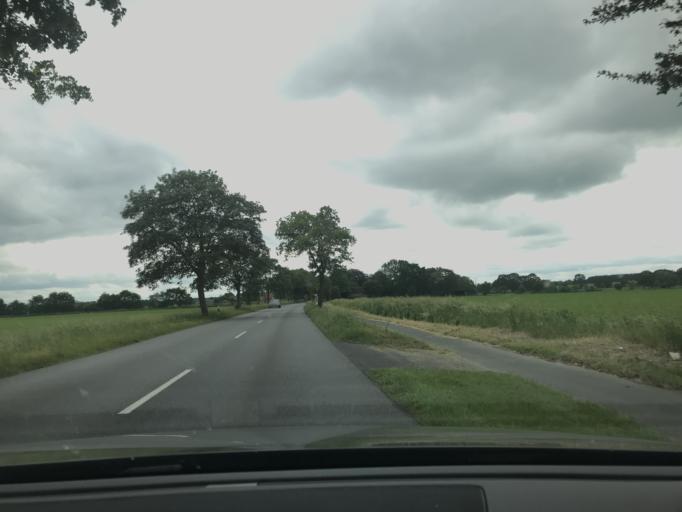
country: DE
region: Lower Saxony
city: Loxstedt
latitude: 53.4625
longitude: 8.6351
